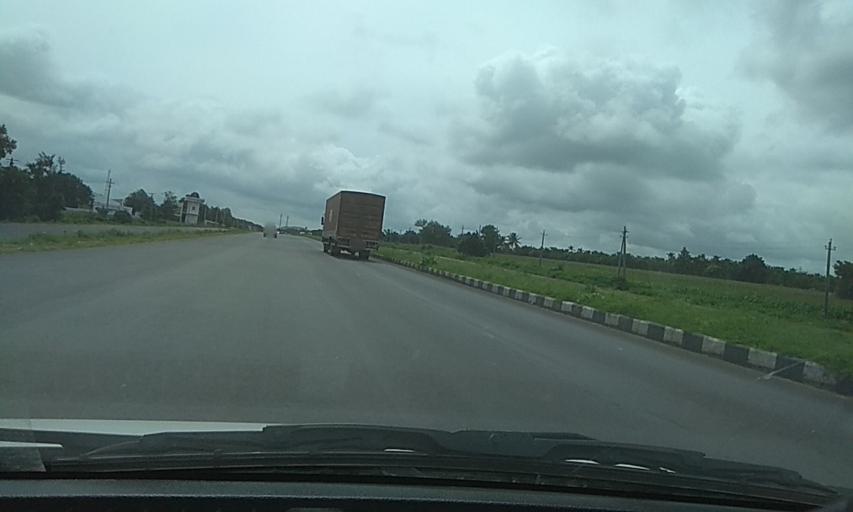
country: IN
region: Karnataka
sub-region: Davanagere
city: Mayakonda
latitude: 14.3815
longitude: 76.0876
